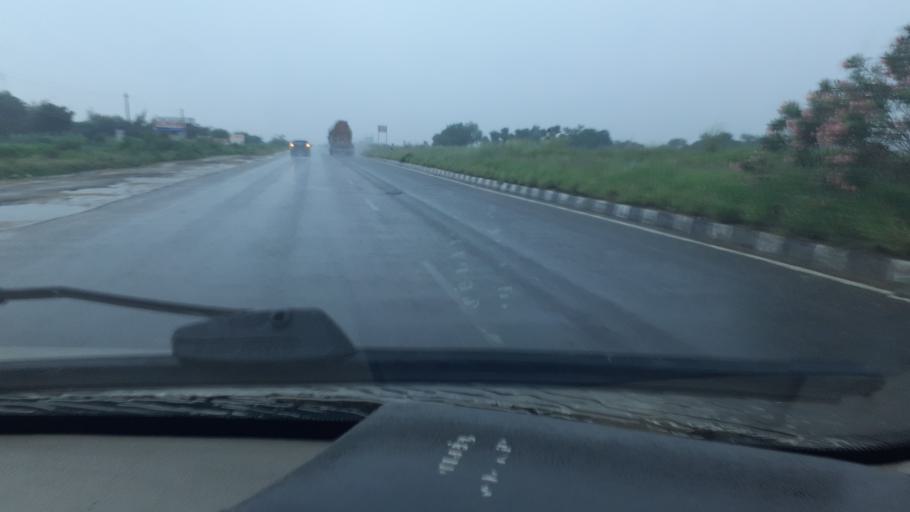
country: IN
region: Tamil Nadu
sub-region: Virudhunagar
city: Sattur
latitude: 9.4125
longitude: 77.9158
